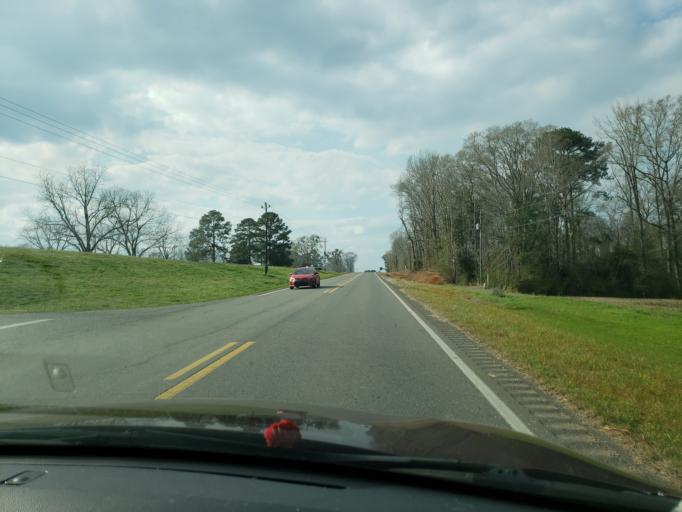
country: US
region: Alabama
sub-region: Hale County
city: Greensboro
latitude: 32.7117
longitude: -87.6129
